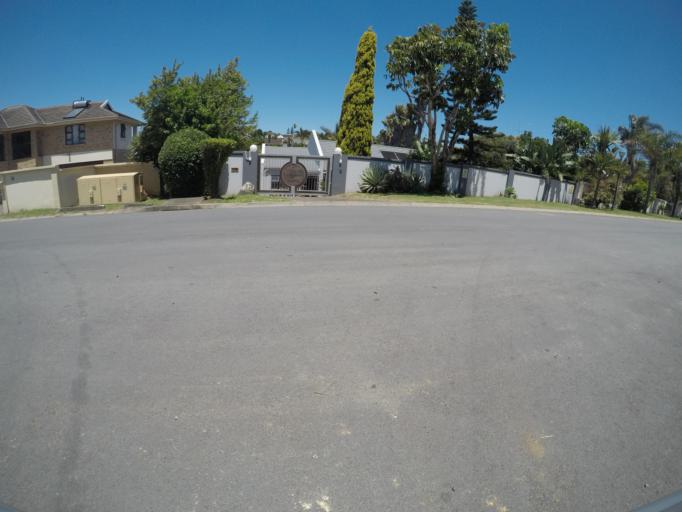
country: ZA
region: Eastern Cape
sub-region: Buffalo City Metropolitan Municipality
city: East London
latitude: -32.9541
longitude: 27.9381
